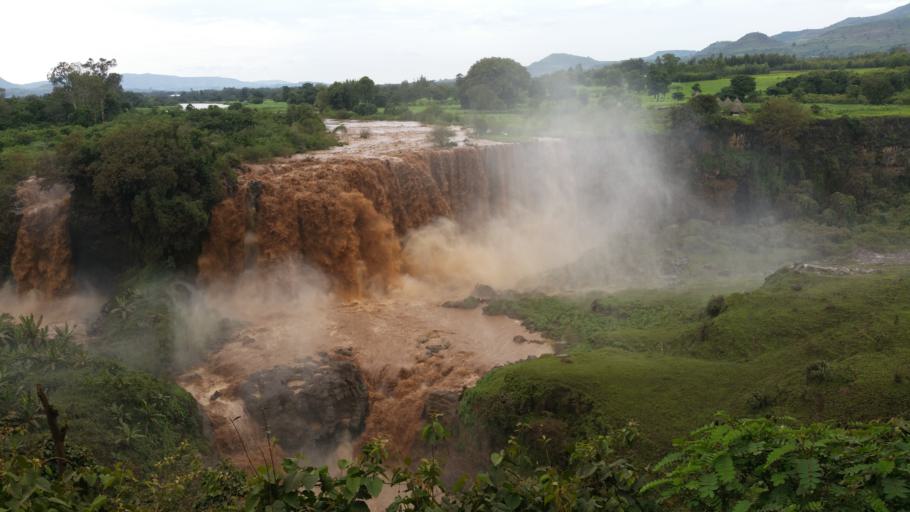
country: ET
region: Amhara
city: Bahir Dar
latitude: 11.4906
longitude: 37.5893
